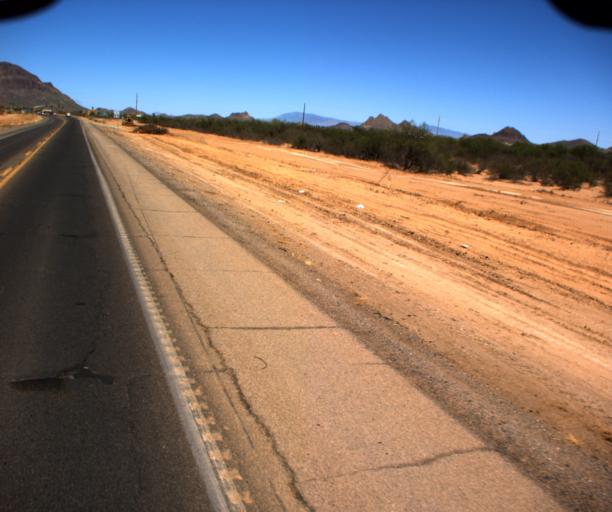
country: US
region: Arizona
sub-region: Pima County
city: Valencia West
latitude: 32.1569
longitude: -111.1100
